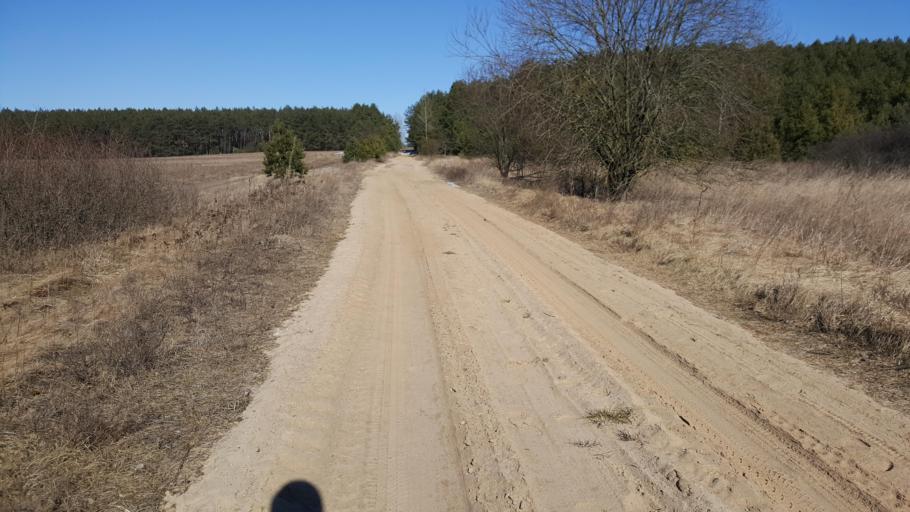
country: BY
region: Brest
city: Kamyanyets
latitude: 52.3770
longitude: 23.8388
